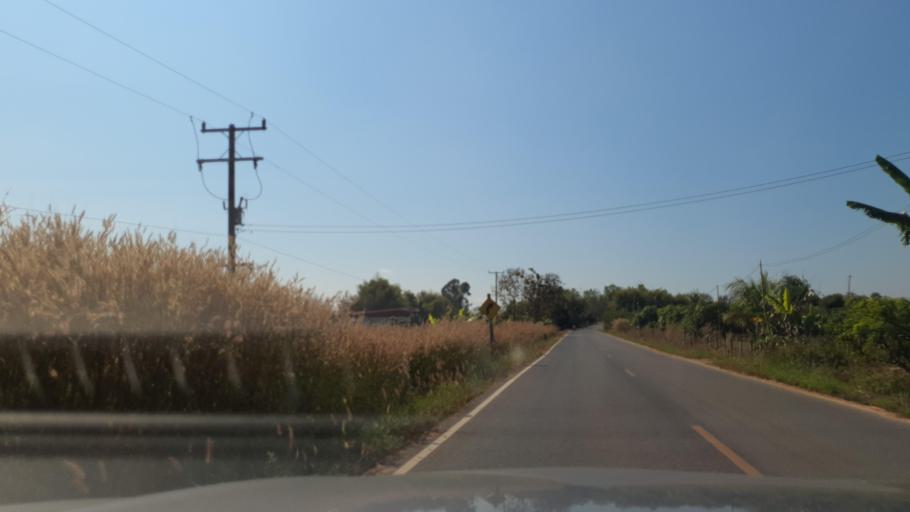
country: TH
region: Nan
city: Pua
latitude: 19.1255
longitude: 100.9217
